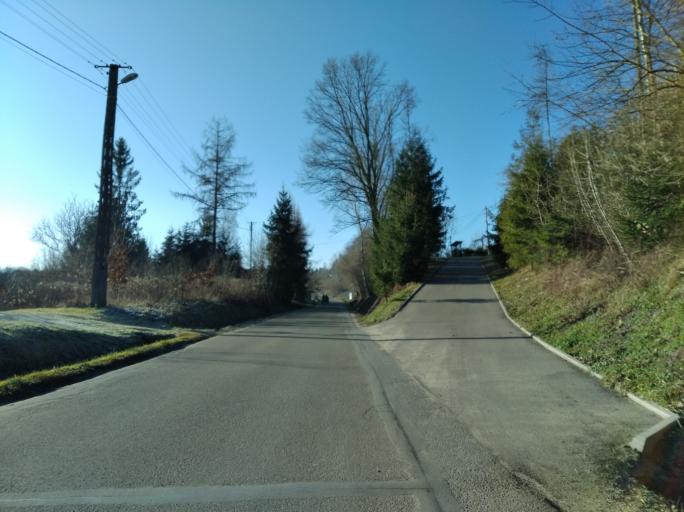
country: PL
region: Subcarpathian Voivodeship
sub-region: Powiat strzyzowski
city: Strzyzow
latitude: 49.8590
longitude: 21.7865
